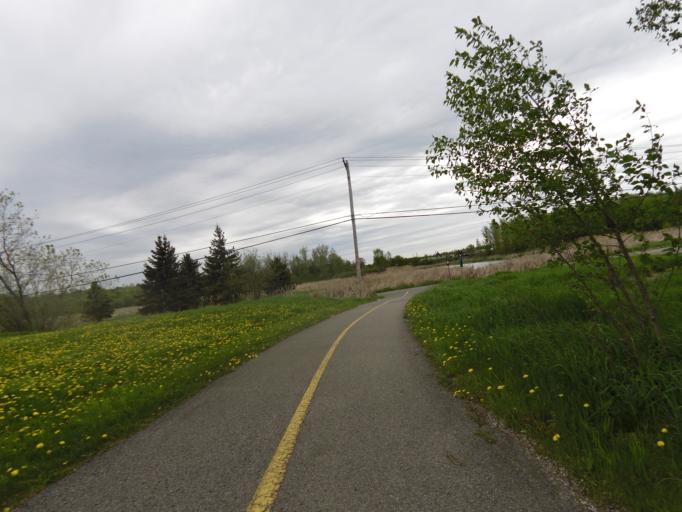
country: CA
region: Quebec
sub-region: Outaouais
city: Gatineau
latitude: 45.4697
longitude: -75.7422
